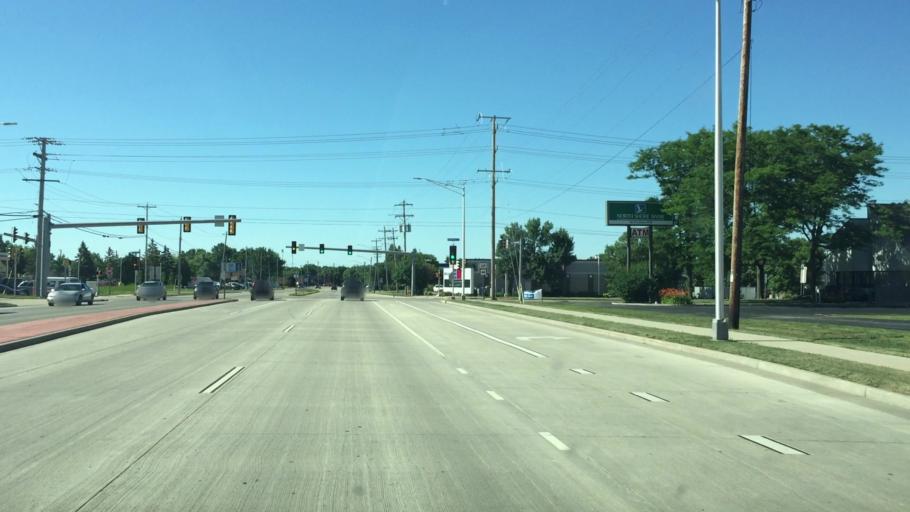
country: US
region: Wisconsin
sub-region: Outagamie County
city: Appleton
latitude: 44.2307
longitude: -88.4242
